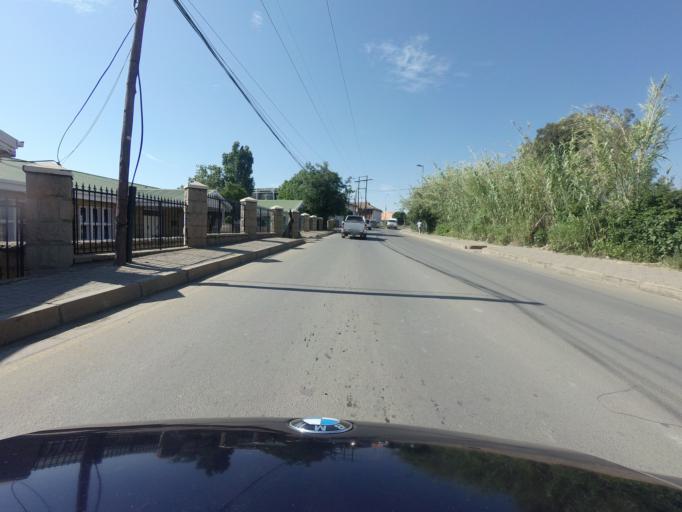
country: LS
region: Maseru
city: Maseru
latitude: -29.3054
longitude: 27.4870
